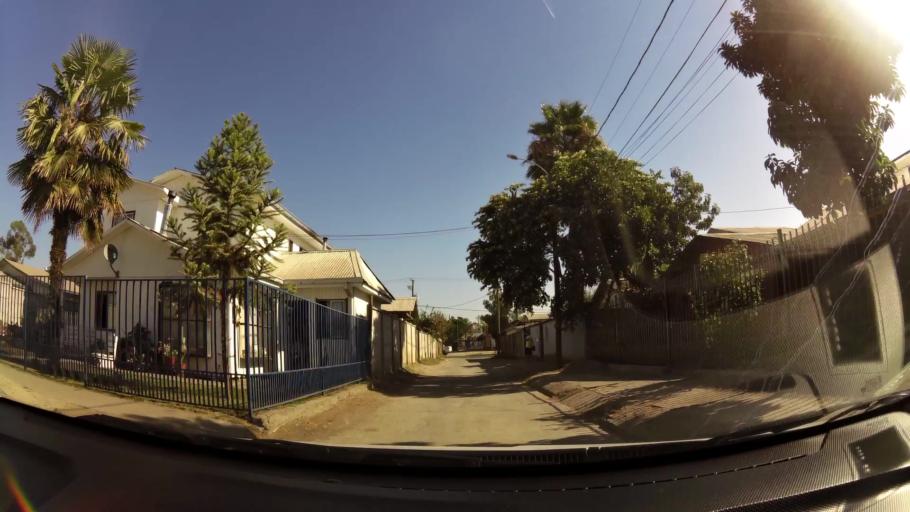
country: CL
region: Maule
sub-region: Provincia de Talca
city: Talca
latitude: -35.4468
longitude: -71.6498
